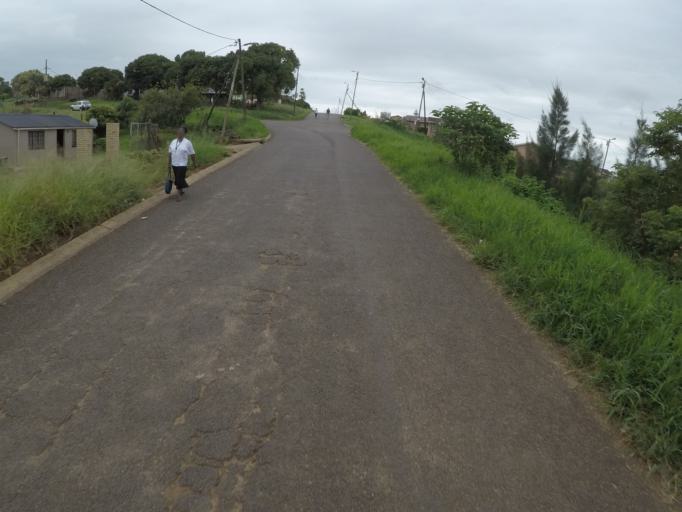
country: ZA
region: KwaZulu-Natal
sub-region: uThungulu District Municipality
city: Empangeni
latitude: -28.7715
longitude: 31.8679
